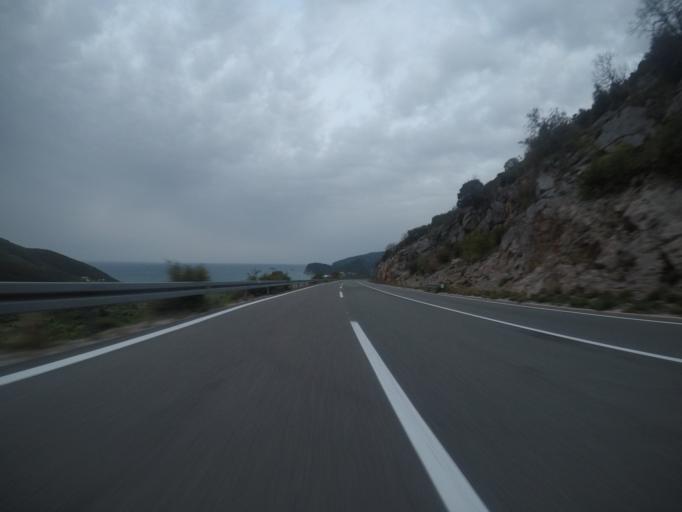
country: ME
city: Petrovac na Moru
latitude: 42.1855
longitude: 18.9905
